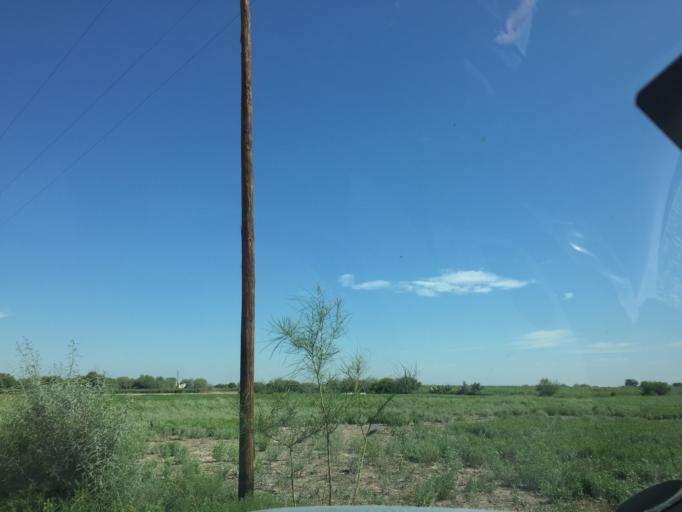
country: MX
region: Durango
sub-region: Gomez Palacio
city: San Felipe
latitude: 25.7252
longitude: -103.3768
